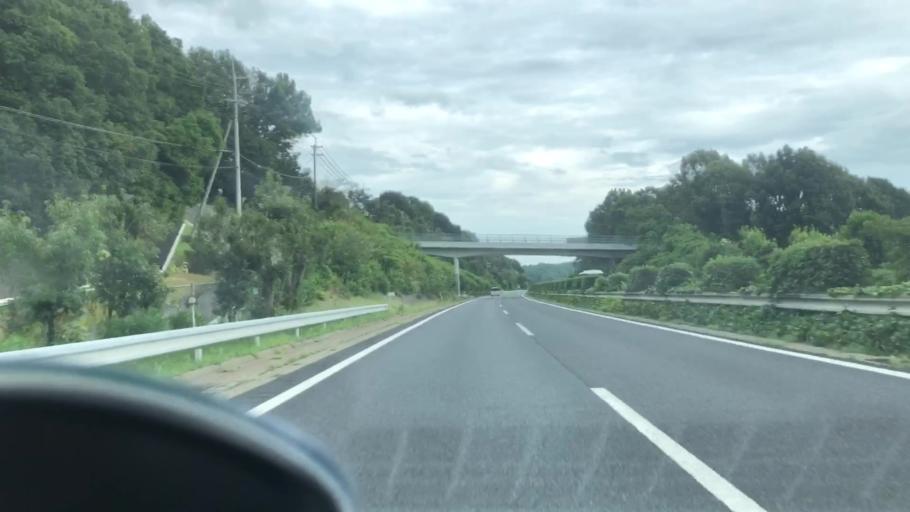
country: JP
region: Hyogo
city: Yashiro
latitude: 34.9306
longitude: 134.9759
